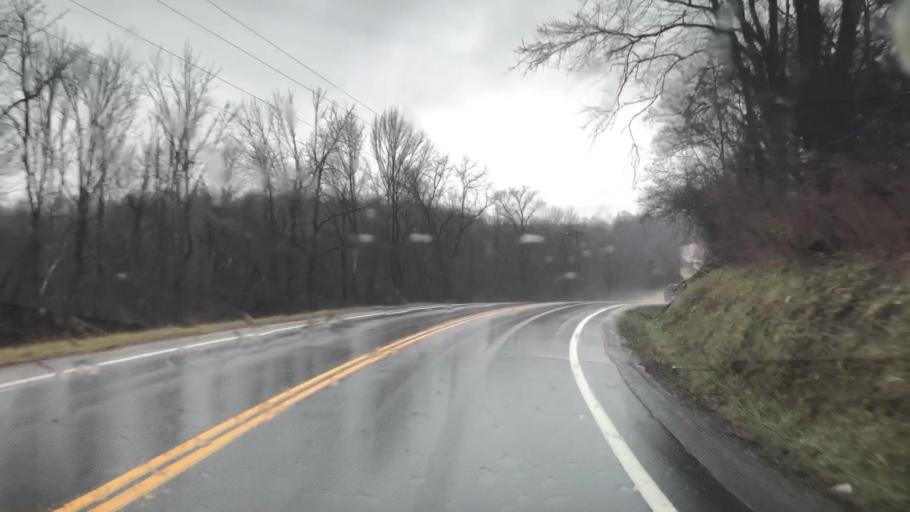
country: US
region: Ohio
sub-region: Harrison County
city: Cadiz
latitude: 40.2144
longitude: -80.9960
